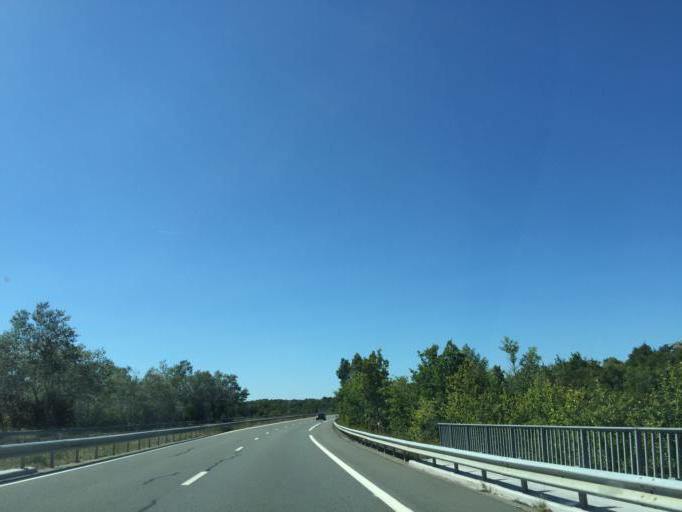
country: FR
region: Languedoc-Roussillon
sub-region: Departement de l'Herault
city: Lodeve
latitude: 43.8892
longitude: 3.2881
